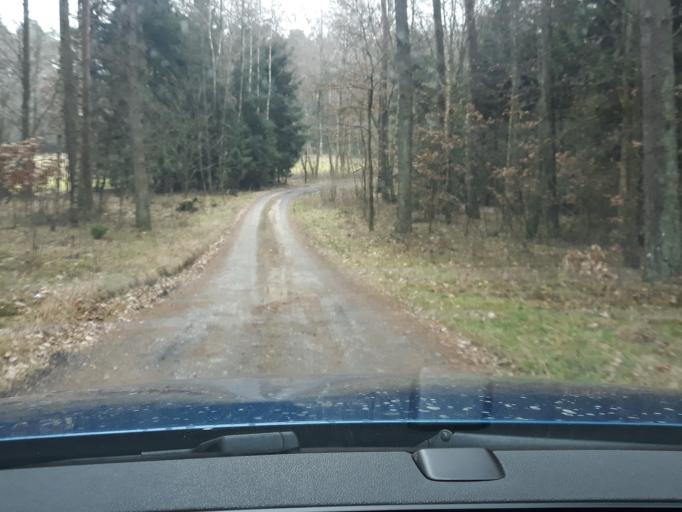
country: PL
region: Pomeranian Voivodeship
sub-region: Powiat czluchowski
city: Czluchow
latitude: 53.8249
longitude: 17.4260
